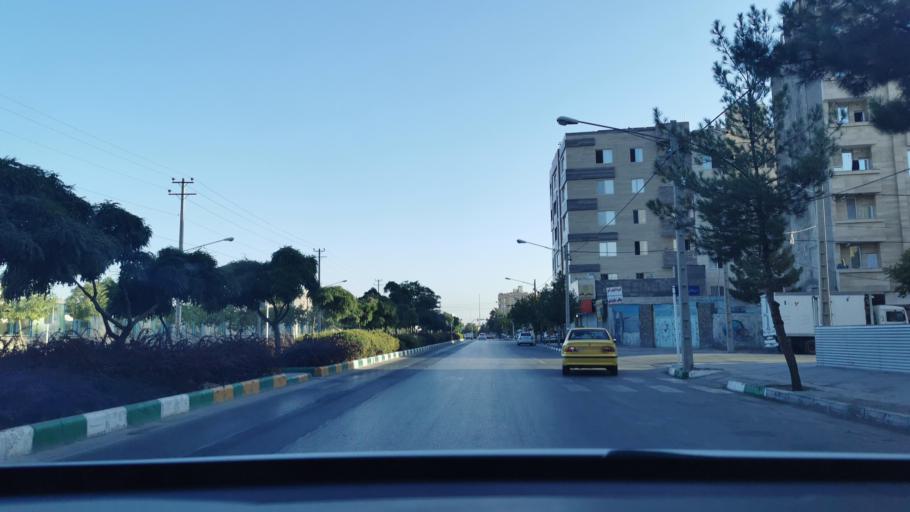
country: IR
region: Razavi Khorasan
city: Mashhad
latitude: 36.3498
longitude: 59.5138
